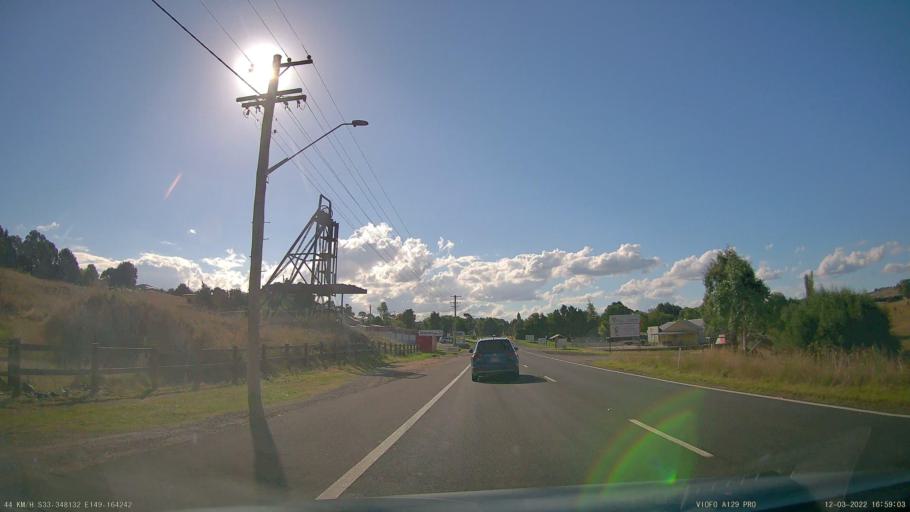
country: AU
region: New South Wales
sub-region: Orange Municipality
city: Orange
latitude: -33.3480
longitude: 149.1641
